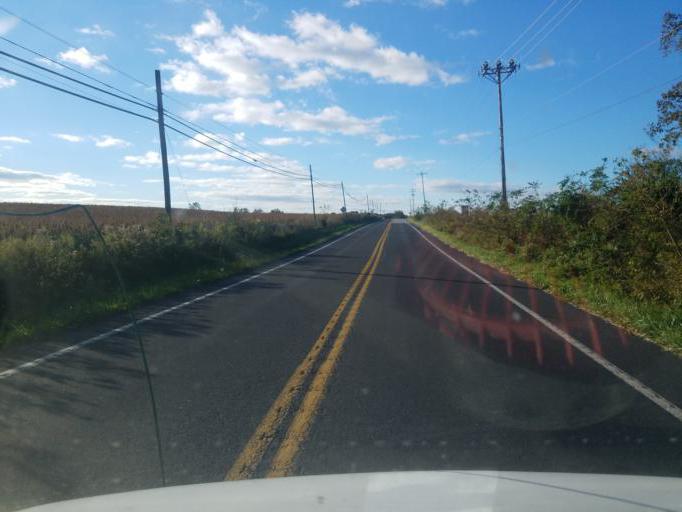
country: US
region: Pennsylvania
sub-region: Adams County
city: Gettysburg
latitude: 39.8467
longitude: -77.2313
